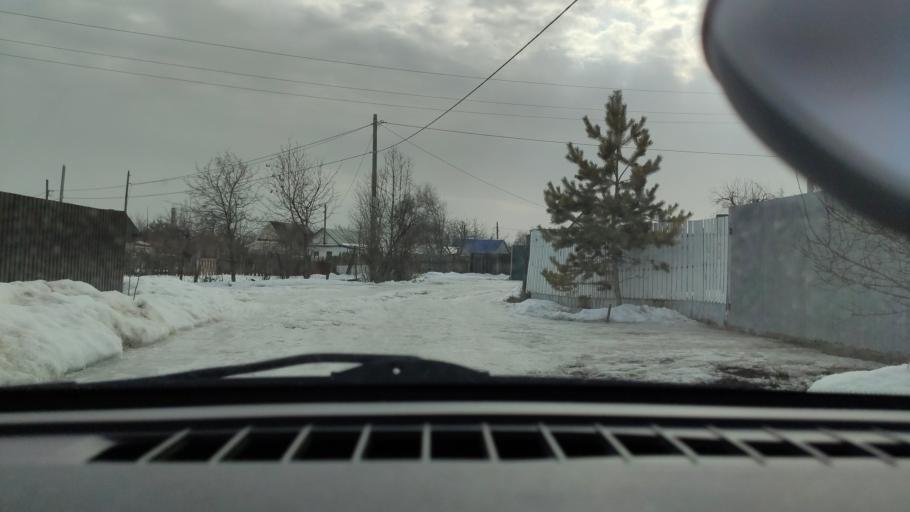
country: RU
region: Samara
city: Petra-Dubrava
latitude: 53.2648
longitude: 50.3060
